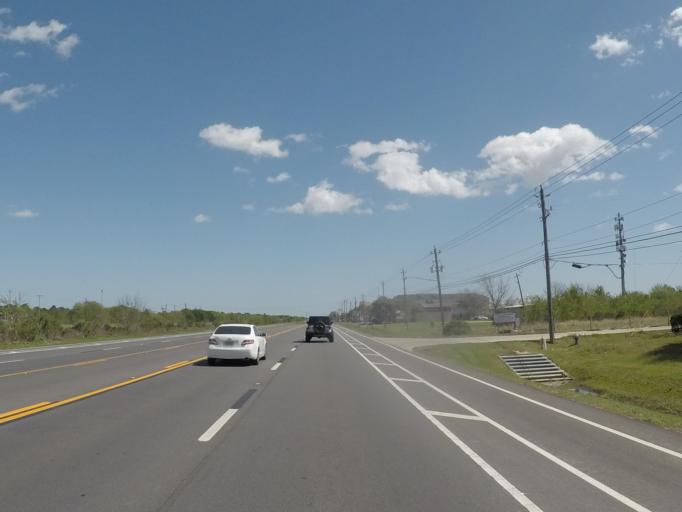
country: US
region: Texas
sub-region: Harris County
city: Webster
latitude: 29.5780
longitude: -95.1559
